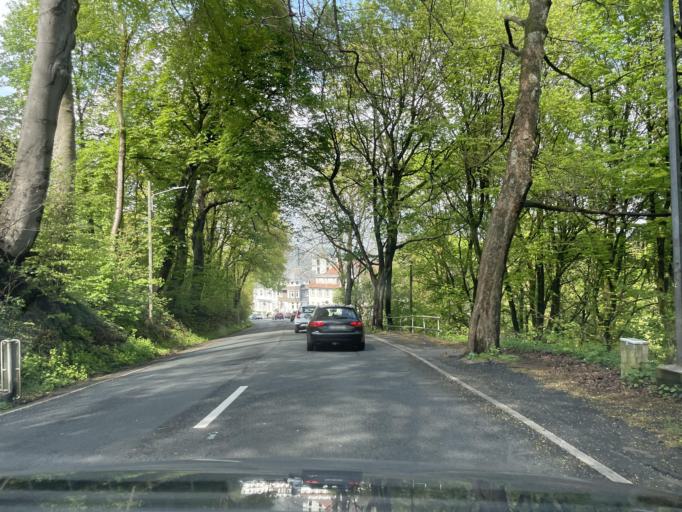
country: DE
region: North Rhine-Westphalia
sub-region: Regierungsbezirk Dusseldorf
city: Wuppertal
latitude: 51.2553
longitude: 7.1777
